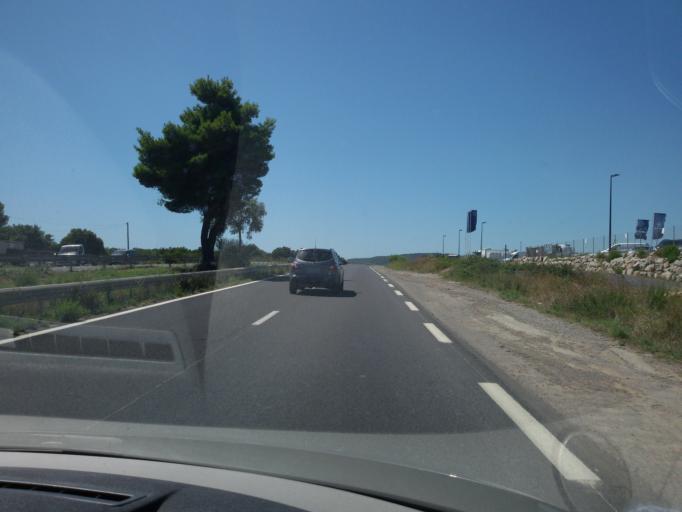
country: FR
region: Languedoc-Roussillon
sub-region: Departement de l'Herault
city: Mireval
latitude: 43.5233
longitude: 3.8150
